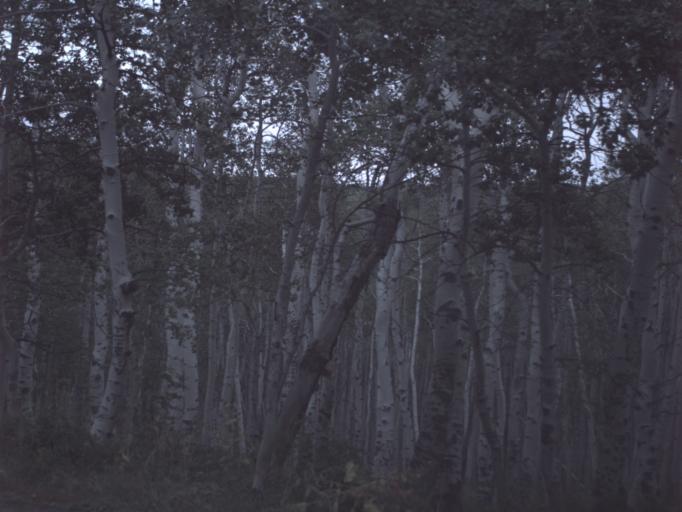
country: US
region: Utah
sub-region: Utah County
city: Lindon
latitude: 40.4184
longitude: -111.6070
